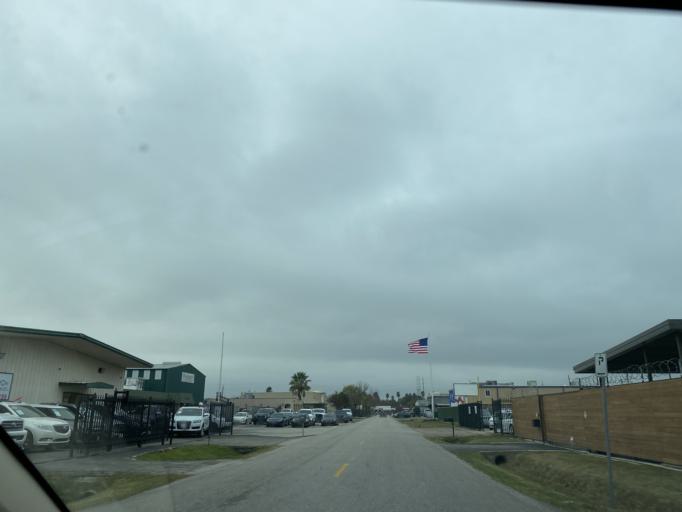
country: US
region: Texas
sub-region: Harris County
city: Bellaire
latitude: 29.7288
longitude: -95.4803
